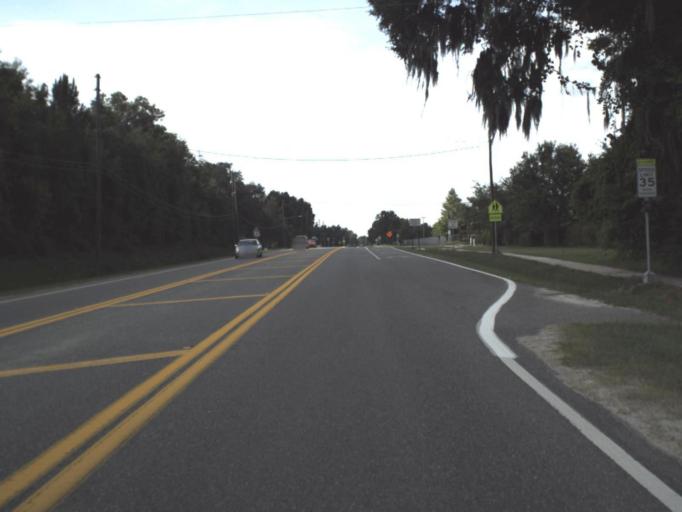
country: US
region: Florida
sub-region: Alachua County
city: High Springs
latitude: 29.9276
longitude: -82.7139
